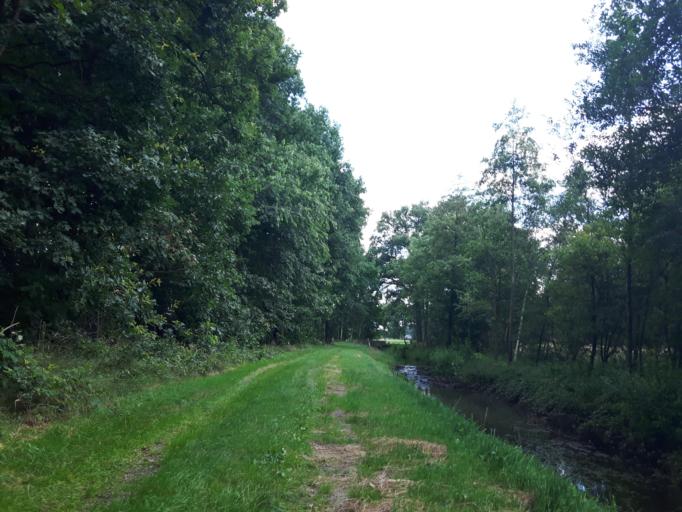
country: NL
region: Overijssel
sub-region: Gemeente Haaksbergen
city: Haaksbergen
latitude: 52.1837
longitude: 6.7732
